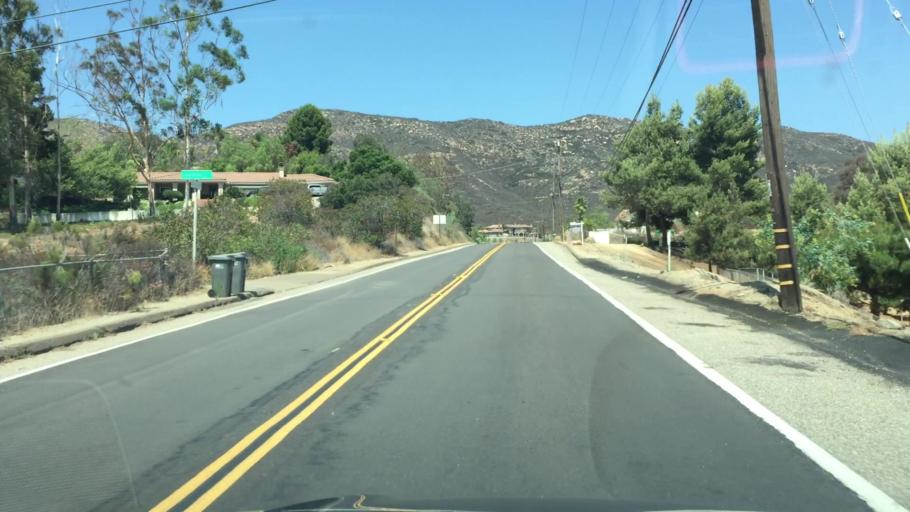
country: US
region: California
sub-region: San Diego County
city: Jamul
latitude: 32.7319
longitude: -116.8542
